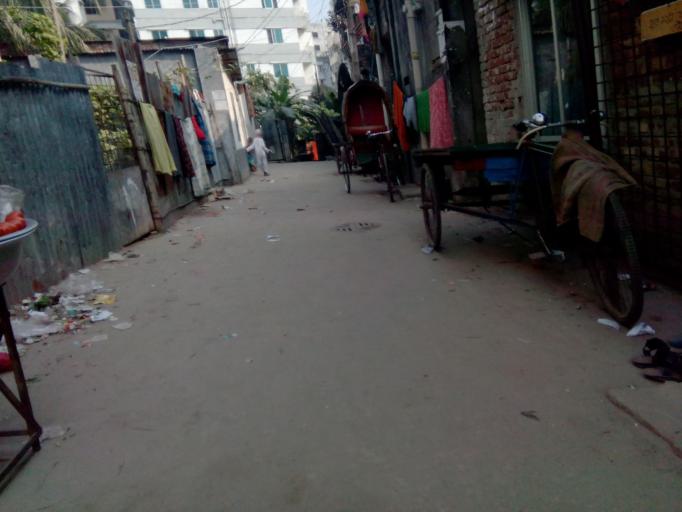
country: BD
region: Dhaka
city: Tungi
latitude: 23.8189
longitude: 90.4255
